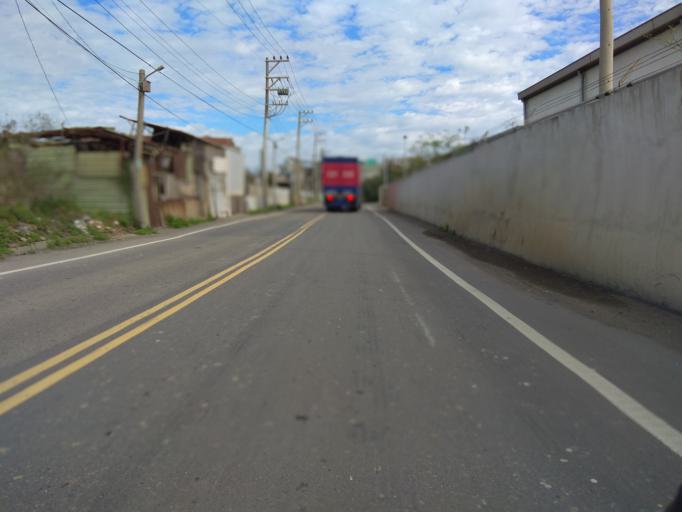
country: TW
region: Taiwan
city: Taoyuan City
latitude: 25.0560
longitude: 121.1013
